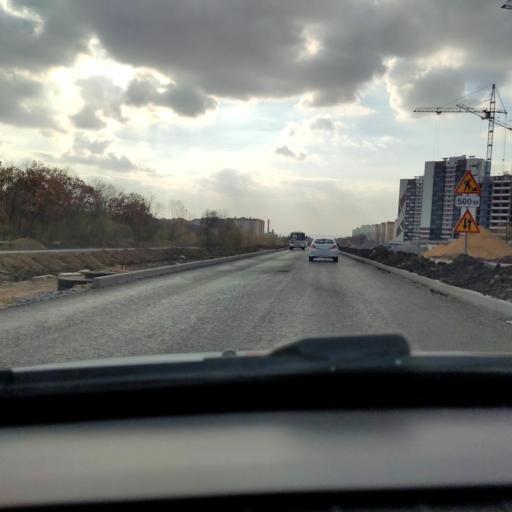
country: RU
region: Voronezj
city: Shilovo
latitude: 51.5664
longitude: 39.1254
